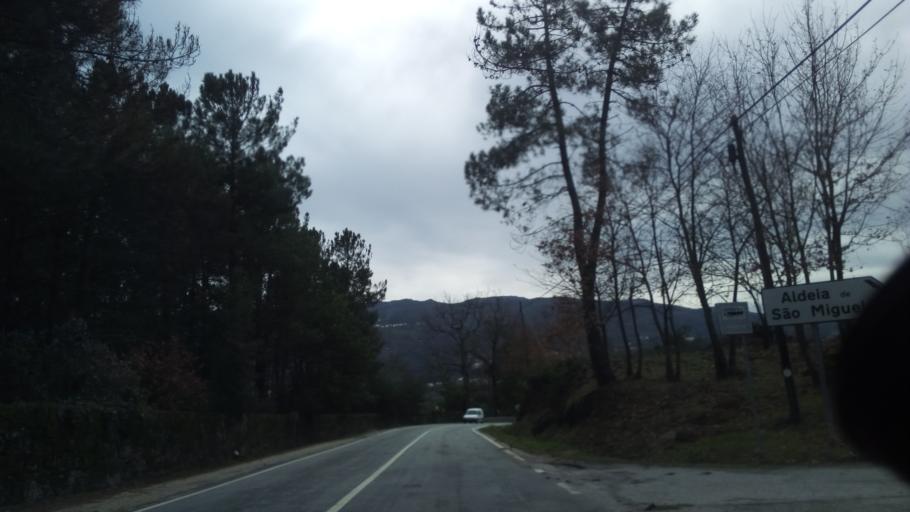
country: PT
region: Guarda
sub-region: Seia
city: Seia
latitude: 40.4422
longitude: -7.7099
